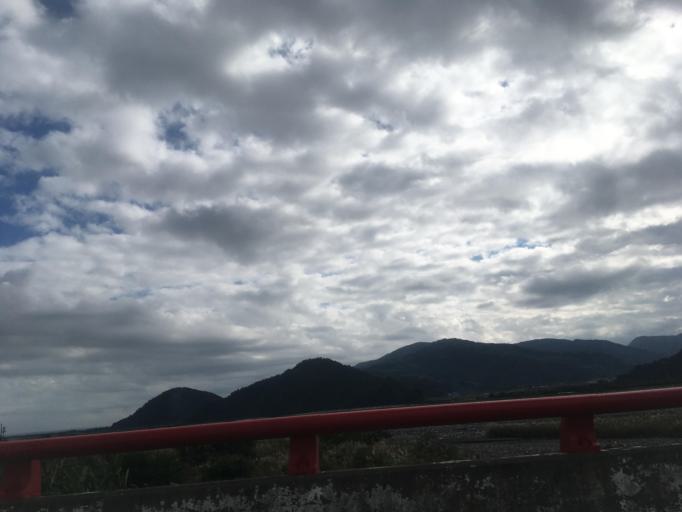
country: TW
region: Taiwan
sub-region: Yilan
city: Yilan
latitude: 24.6538
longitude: 121.5800
